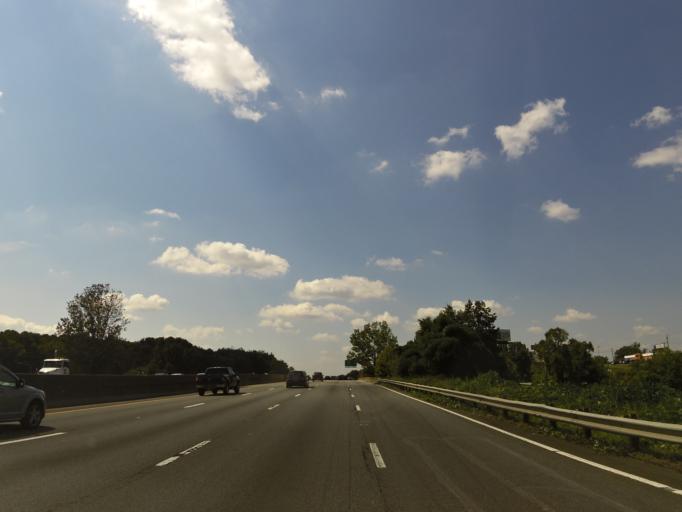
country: US
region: North Carolina
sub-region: Gaston County
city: Gastonia
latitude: 35.2833
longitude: -81.1863
